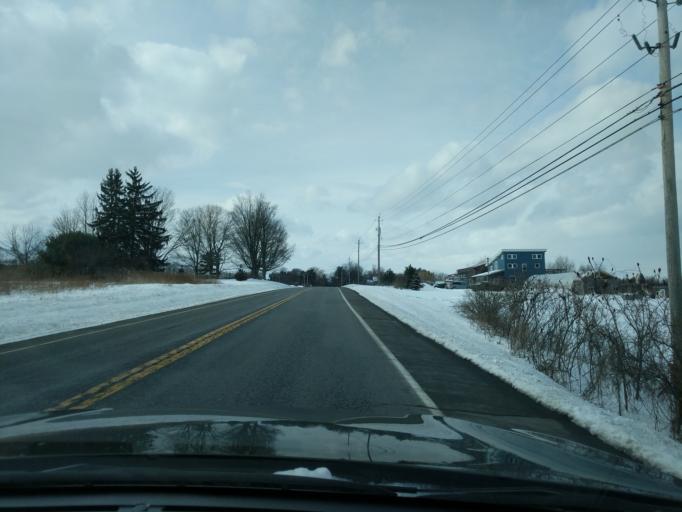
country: US
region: New York
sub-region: Tompkins County
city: Northwest Ithaca
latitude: 42.4865
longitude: -76.5749
